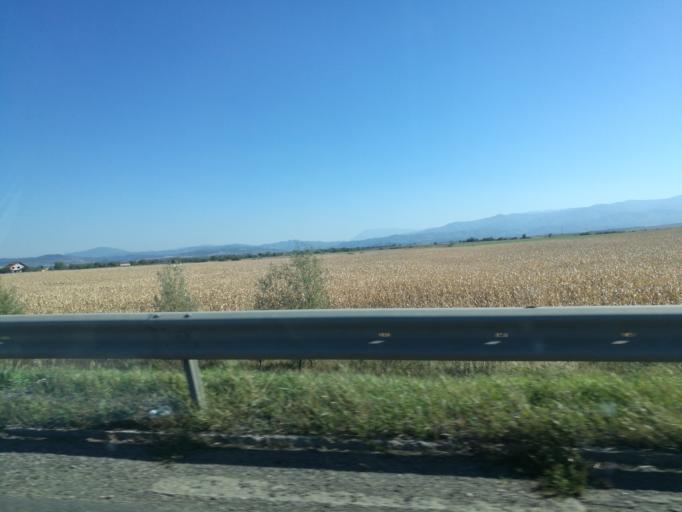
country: RO
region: Brasov
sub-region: Comuna Sercaia
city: Sercaia
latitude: 45.8255
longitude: 25.1047
